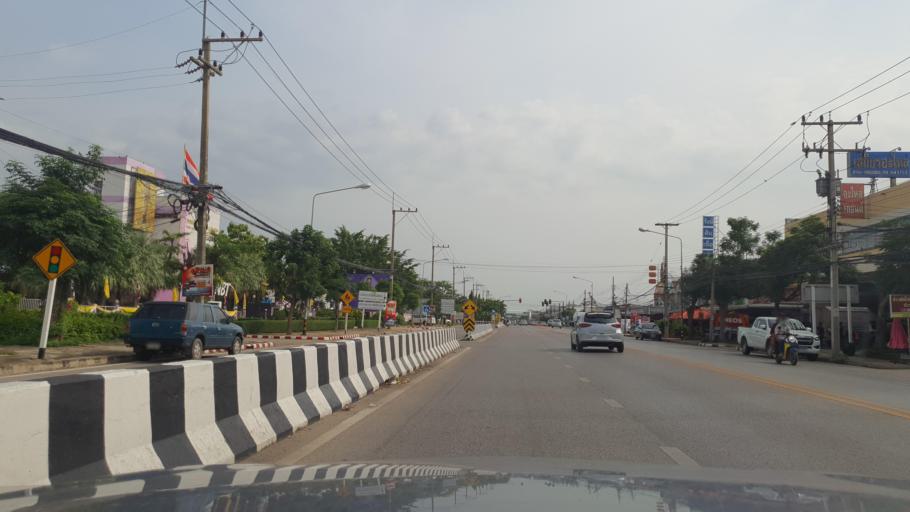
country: TH
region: Phitsanulok
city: Phitsanulok
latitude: 16.8406
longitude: 100.2657
